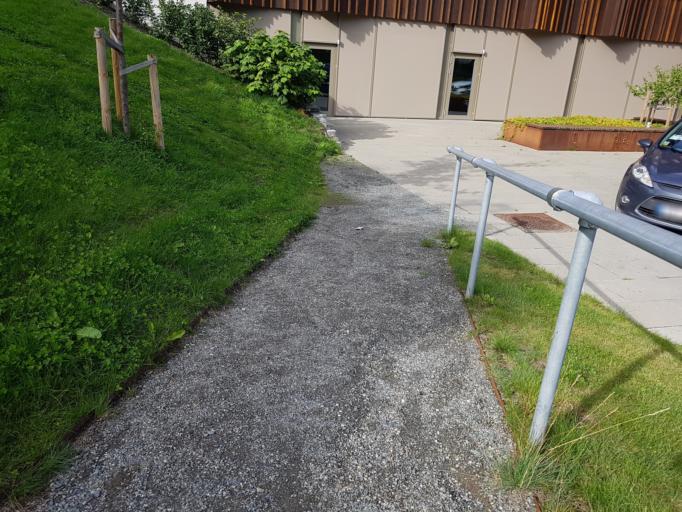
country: NO
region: Sor-Trondelag
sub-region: Trondheim
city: Trondheim
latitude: 63.4288
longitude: 10.4389
